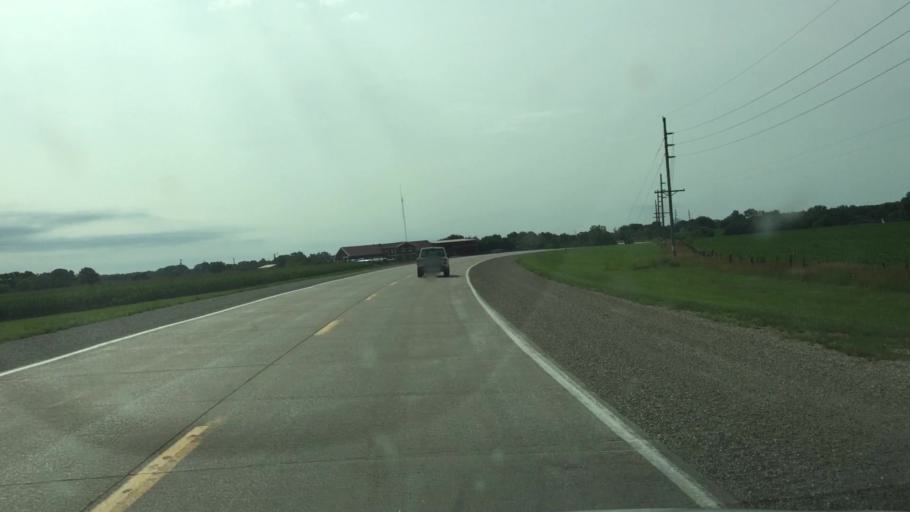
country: US
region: Illinois
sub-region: Hancock County
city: Nauvoo
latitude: 40.6381
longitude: -91.5214
